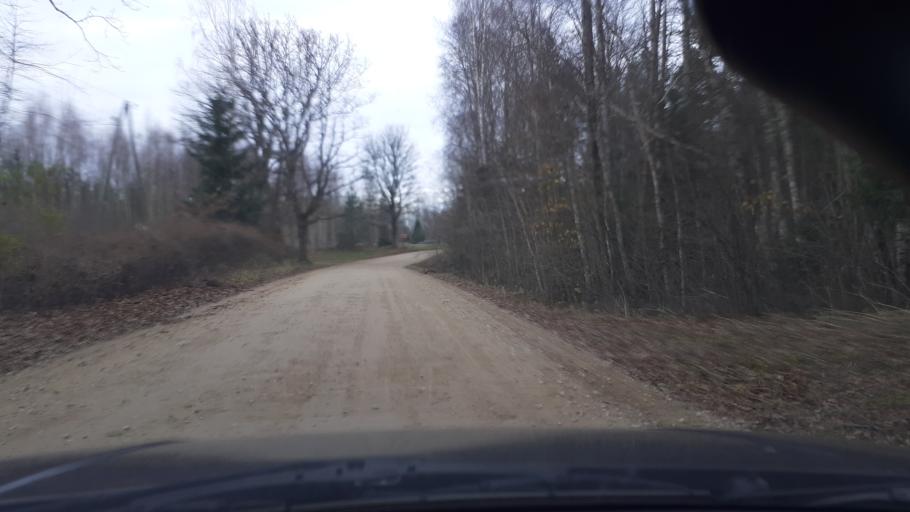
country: LV
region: Alsunga
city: Alsunga
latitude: 56.9483
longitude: 21.6415
